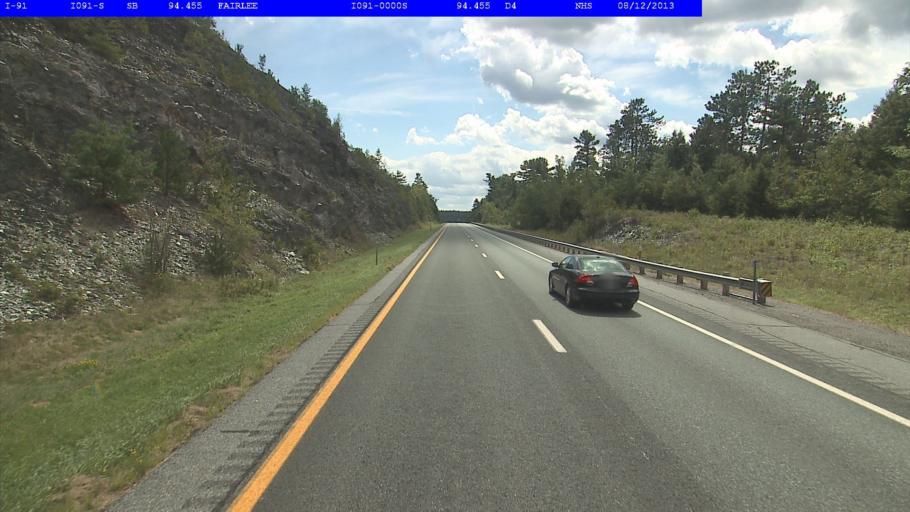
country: US
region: New Hampshire
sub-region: Grafton County
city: Orford
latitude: 43.9398
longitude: -72.1331
